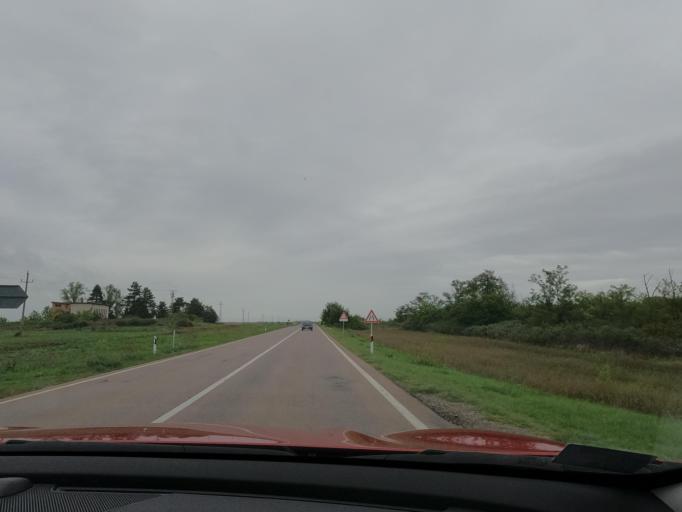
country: RS
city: Banatska Topola
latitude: 45.7184
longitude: 20.4182
